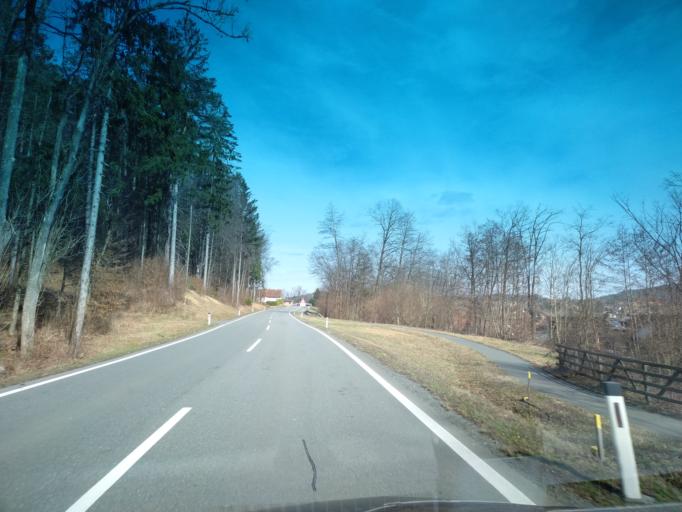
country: AT
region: Styria
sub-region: Politischer Bezirk Deutschlandsberg
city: Wettmannstatten
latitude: 46.8261
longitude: 15.4041
